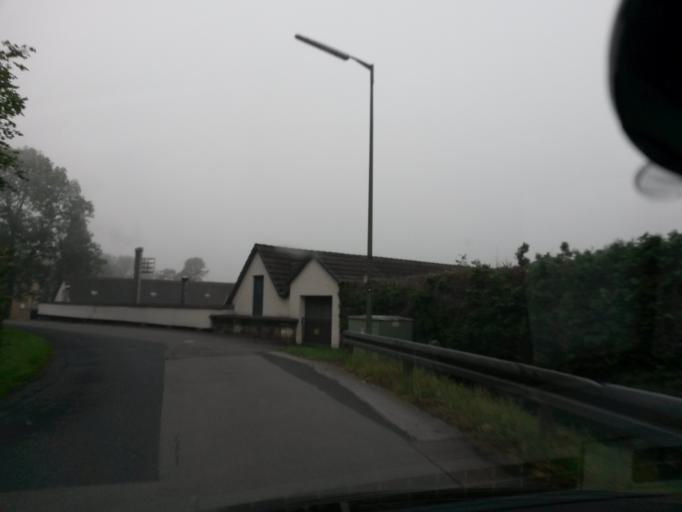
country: DE
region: North Rhine-Westphalia
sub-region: Regierungsbezirk Koln
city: Engelskirchen
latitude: 50.9859
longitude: 7.4294
